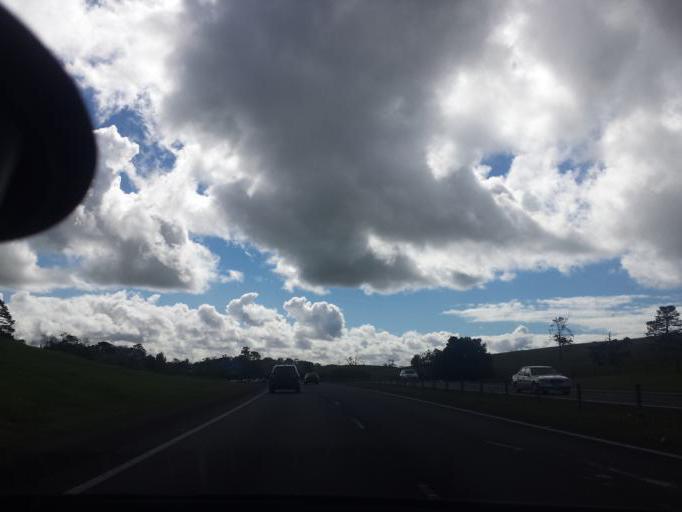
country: NZ
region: Auckland
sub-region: Auckland
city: Rothesay Bay
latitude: -36.6727
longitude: 174.6830
